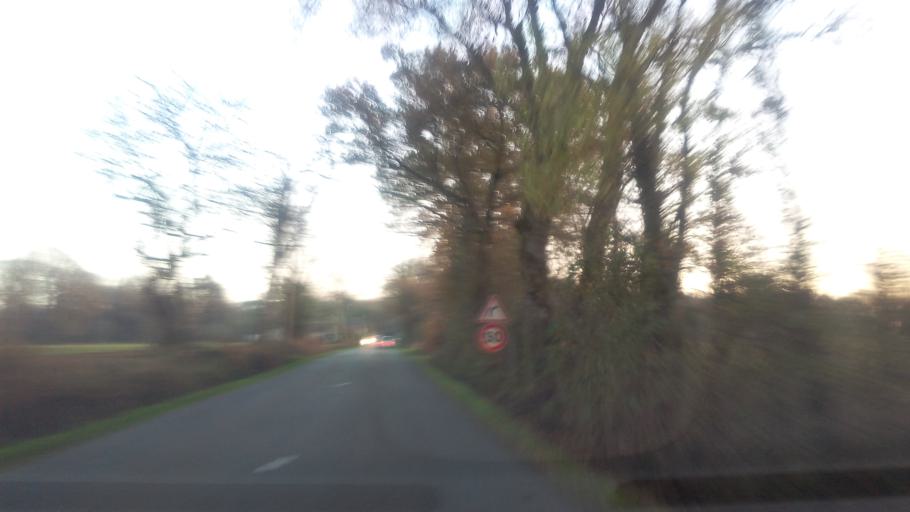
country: FR
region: Brittany
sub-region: Departement d'Ille-et-Vilaine
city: Bains-sur-Oust
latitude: 47.7112
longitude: -2.0539
